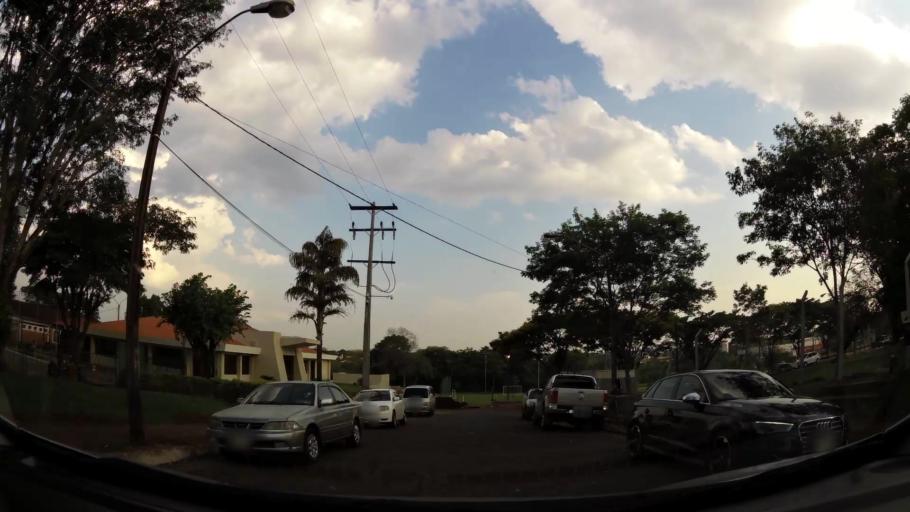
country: PY
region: Alto Parana
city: Presidente Franco
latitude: -25.5234
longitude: -54.6374
